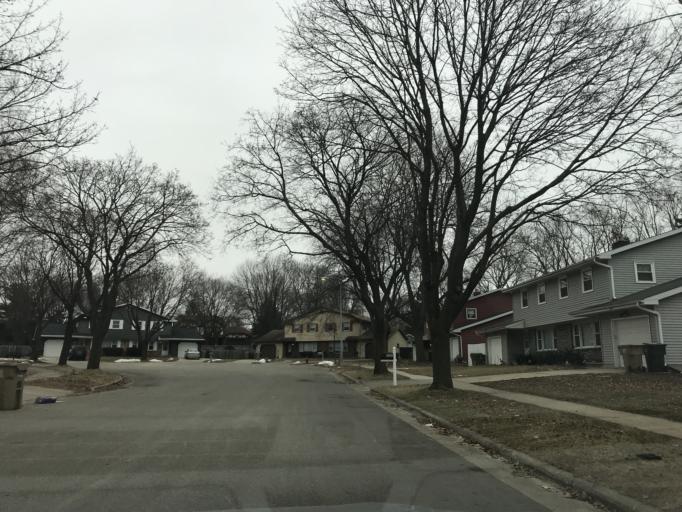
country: US
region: Wisconsin
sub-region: Dane County
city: Monona
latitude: 43.0999
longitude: -89.2903
